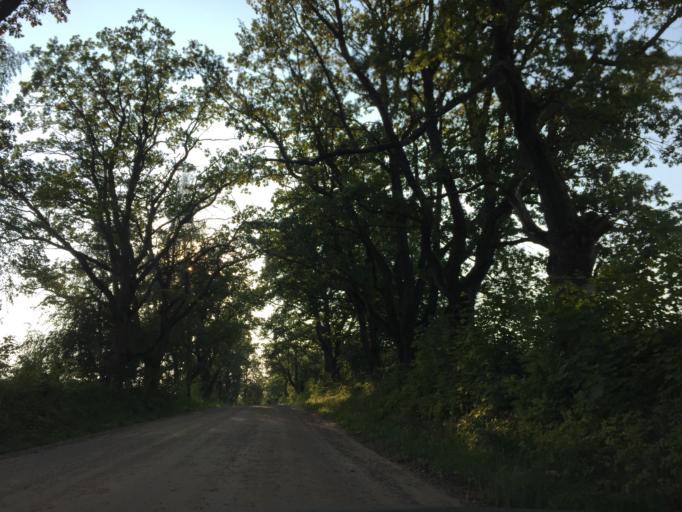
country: LV
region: Limbazu Rajons
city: Limbazi
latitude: 57.5504
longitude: 24.7887
